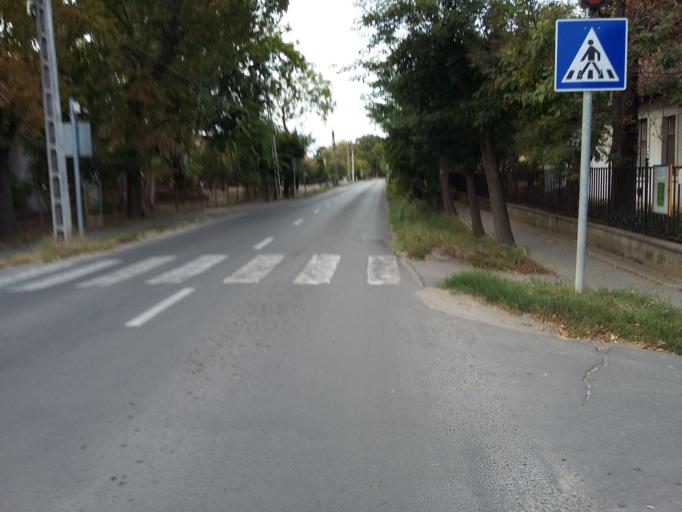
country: HU
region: Csongrad
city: Szeged
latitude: 46.2287
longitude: 20.1158
